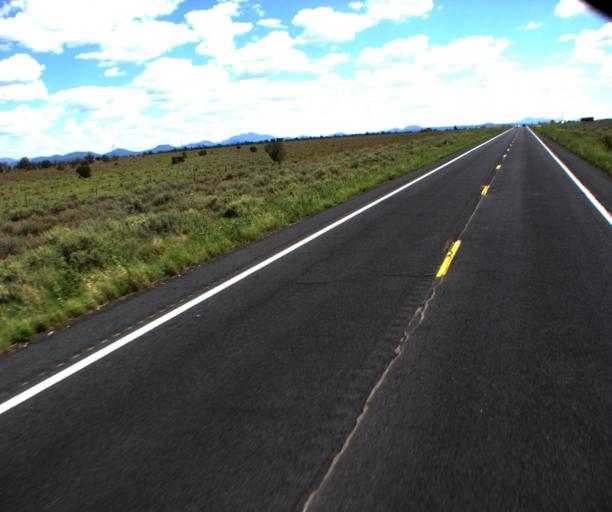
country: US
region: Arizona
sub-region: Coconino County
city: Grand Canyon Village
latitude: 35.6692
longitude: -112.1372
